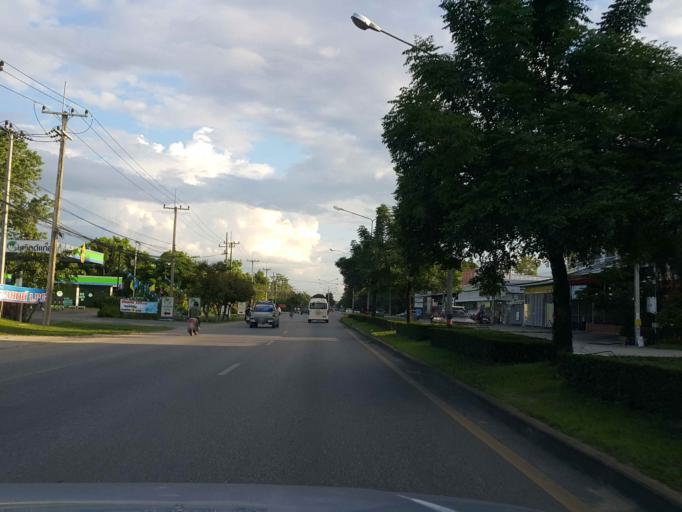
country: TH
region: Chiang Mai
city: San Sai
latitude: 18.8378
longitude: 99.0128
